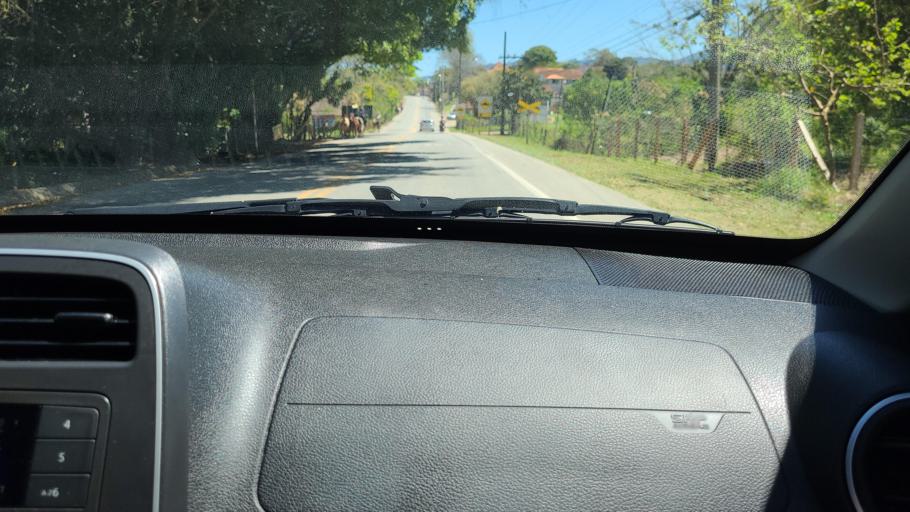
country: BR
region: Sao Paulo
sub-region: Tremembe
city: Tremembe
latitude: -22.8850
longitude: -45.5281
